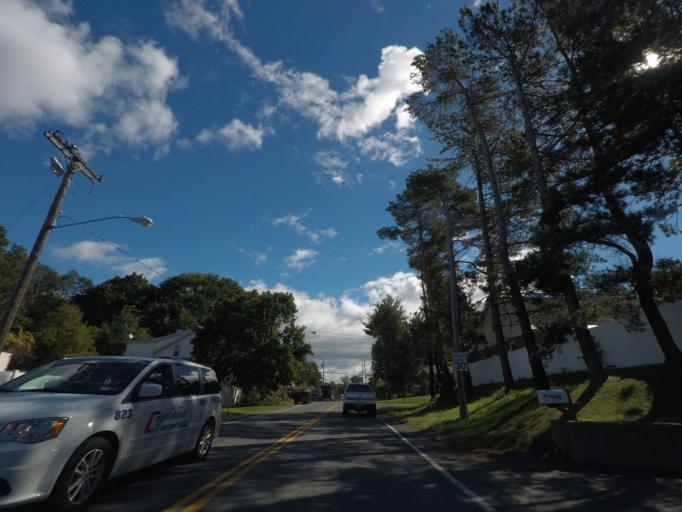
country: US
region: New York
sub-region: Albany County
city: Menands
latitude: 42.7092
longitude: -73.7157
